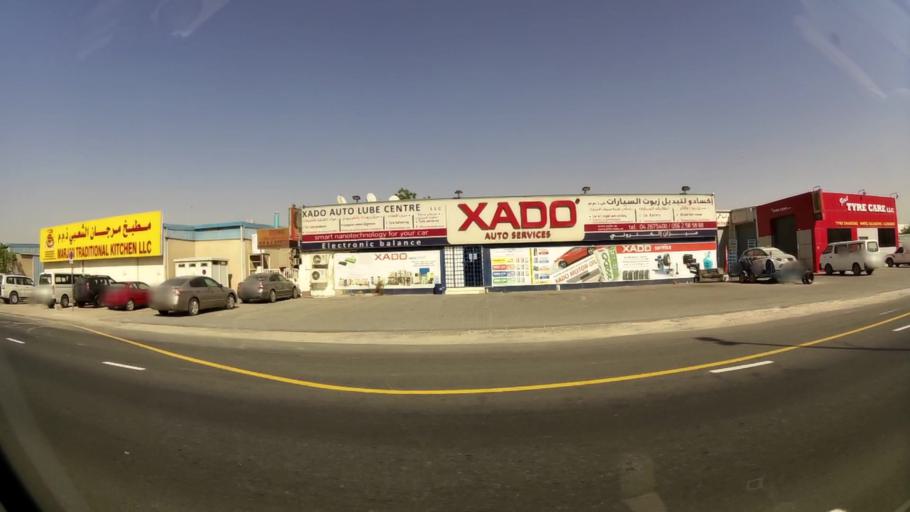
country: AE
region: Ash Shariqah
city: Sharjah
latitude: 25.2927
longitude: 55.3863
